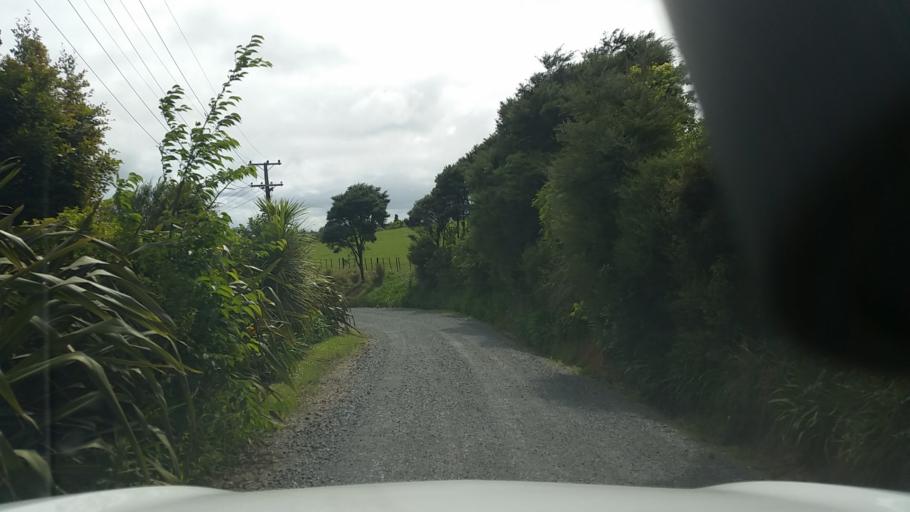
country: NZ
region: Auckland
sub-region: Auckland
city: Muriwai Beach
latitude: -36.8469
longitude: 174.5226
